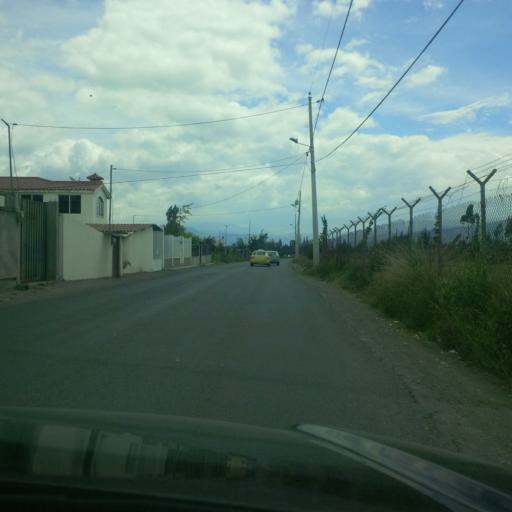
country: EC
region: Chimborazo
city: Riobamba
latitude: -1.6437
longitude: -78.6521
